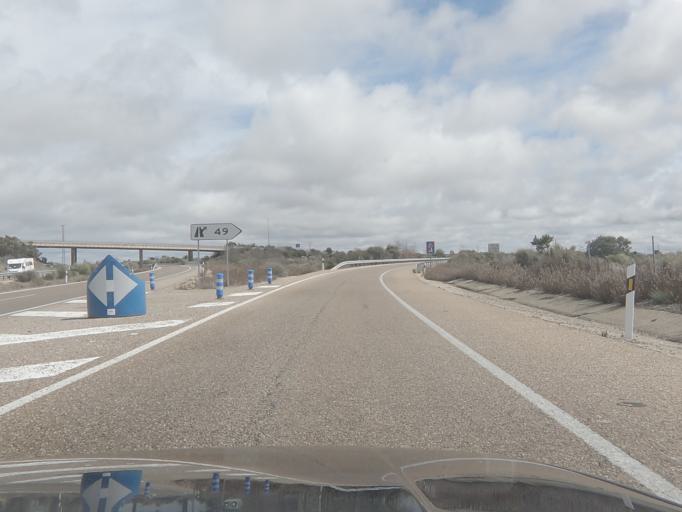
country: ES
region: Castille and Leon
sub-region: Provincia de Zamora
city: Villardeciervos
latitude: 42.0055
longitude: -6.2583
